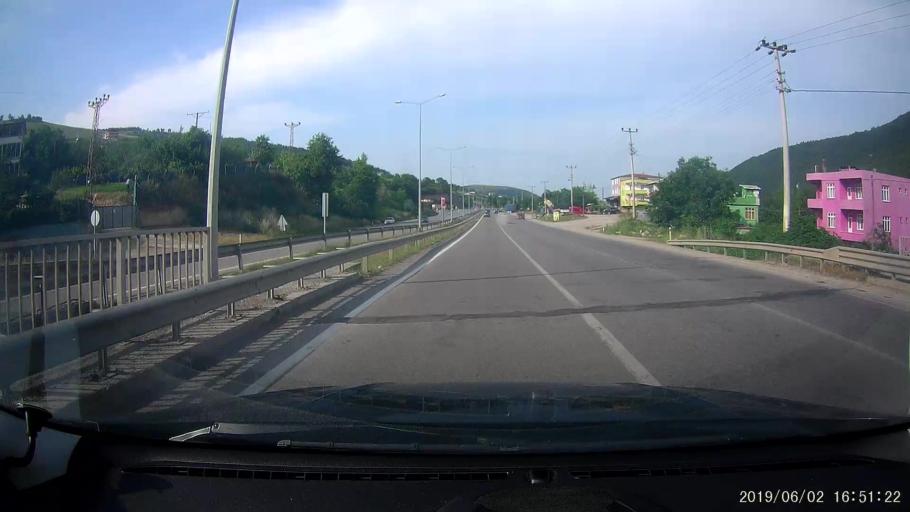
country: TR
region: Samsun
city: Taflan
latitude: 41.2729
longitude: 36.1815
